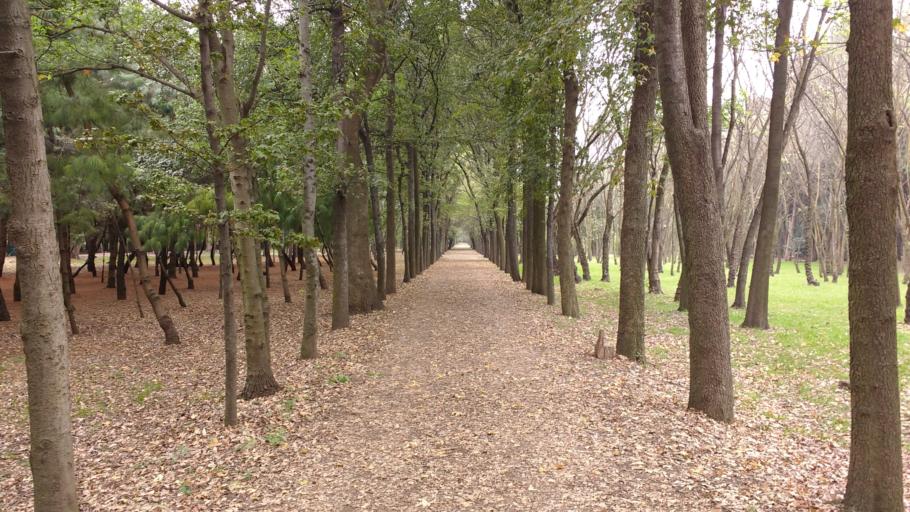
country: MX
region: Mexico City
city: Coyoacan
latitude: 19.3524
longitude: -99.1716
